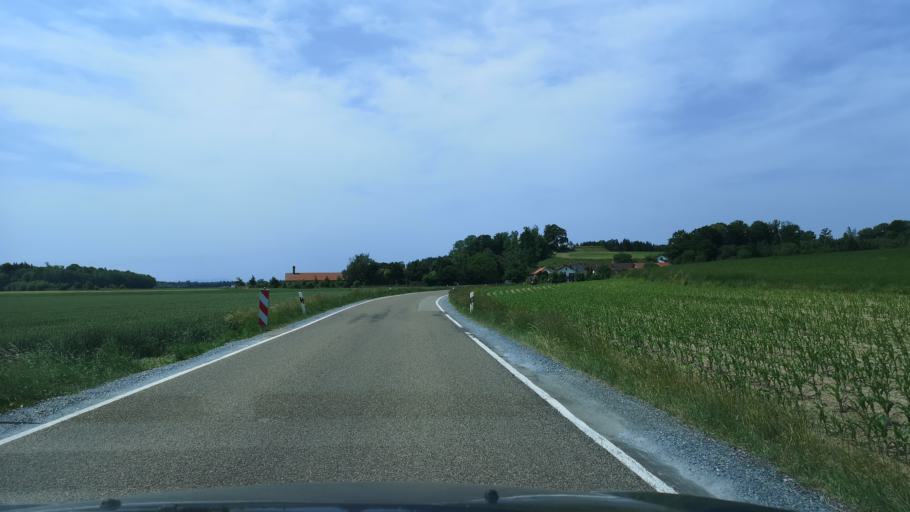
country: DE
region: Bavaria
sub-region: Upper Bavaria
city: Anzing
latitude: 48.1404
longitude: 11.8507
